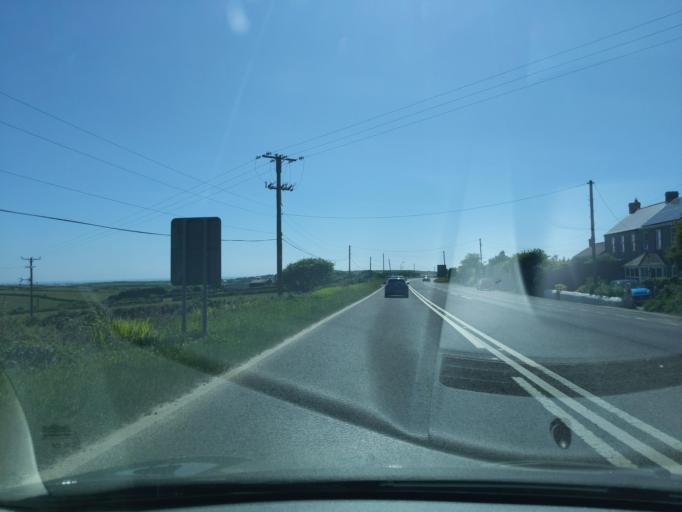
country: GB
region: England
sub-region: Cornwall
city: Wendron
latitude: 50.1520
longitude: -5.1966
